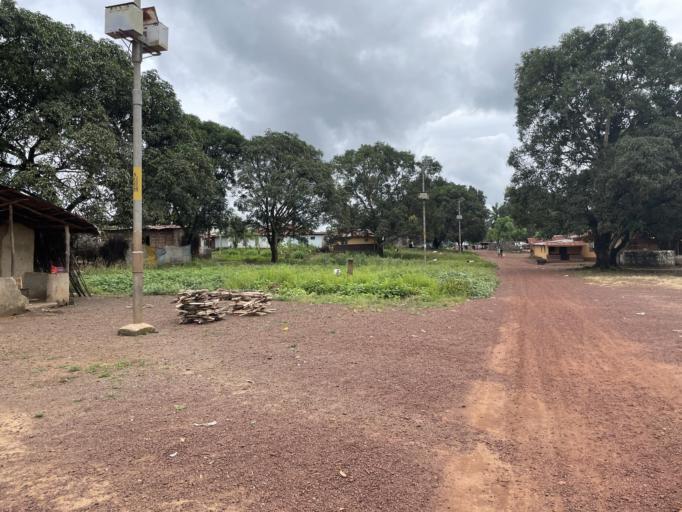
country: SL
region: Northern Province
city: Kambia
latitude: 9.1293
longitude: -12.9091
